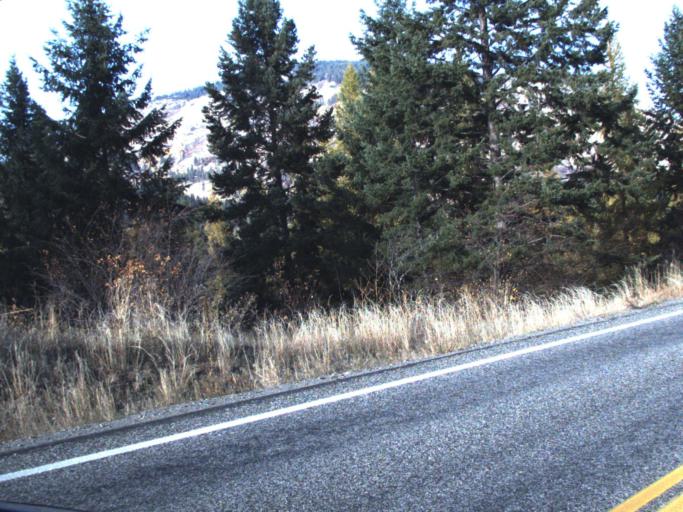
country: CA
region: British Columbia
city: Rossland
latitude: 48.8613
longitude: -117.8760
